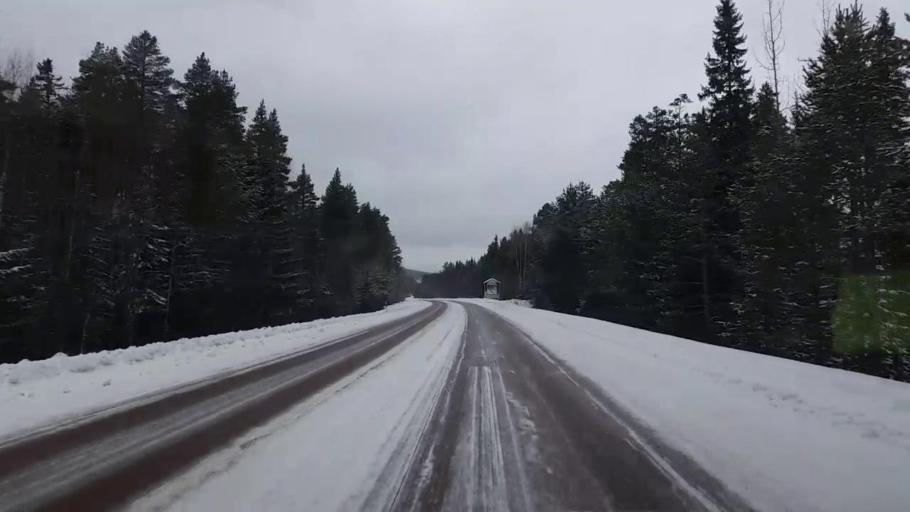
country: SE
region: Jaemtland
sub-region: Bergs Kommun
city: Hoverberg
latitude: 62.4561
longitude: 14.5480
